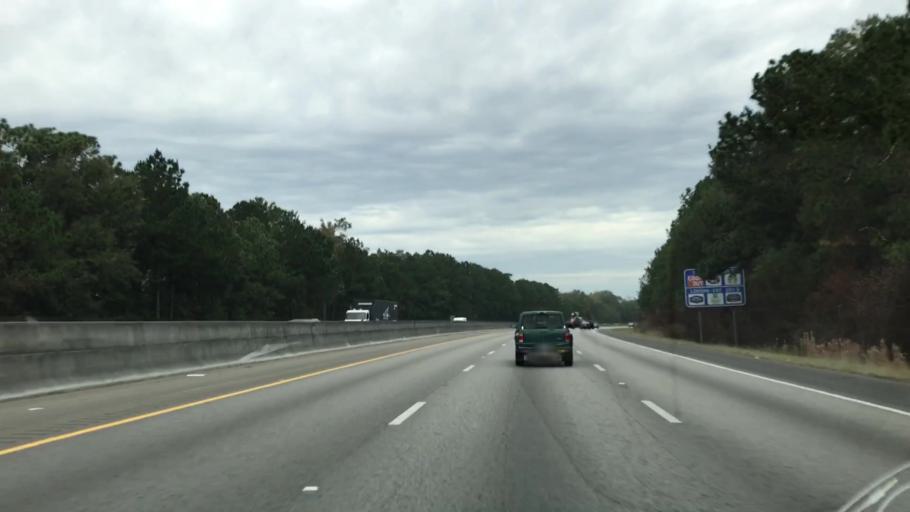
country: US
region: South Carolina
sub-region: Berkeley County
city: Ladson
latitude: 32.9634
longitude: -80.0733
